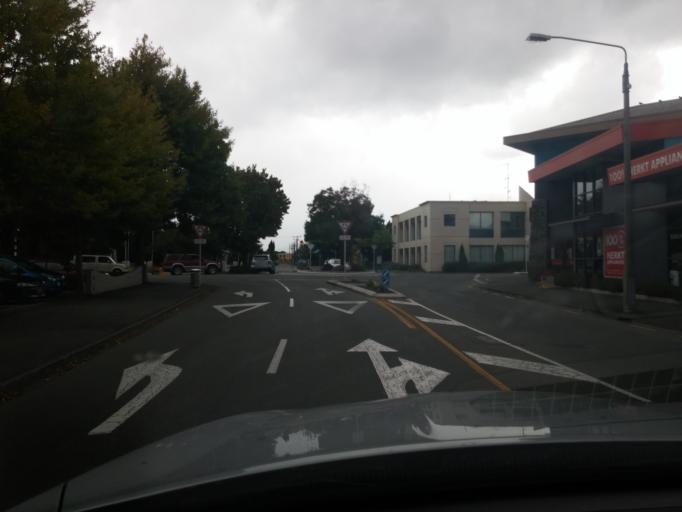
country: NZ
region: Marlborough
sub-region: Marlborough District
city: Blenheim
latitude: -41.5123
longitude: 173.9544
